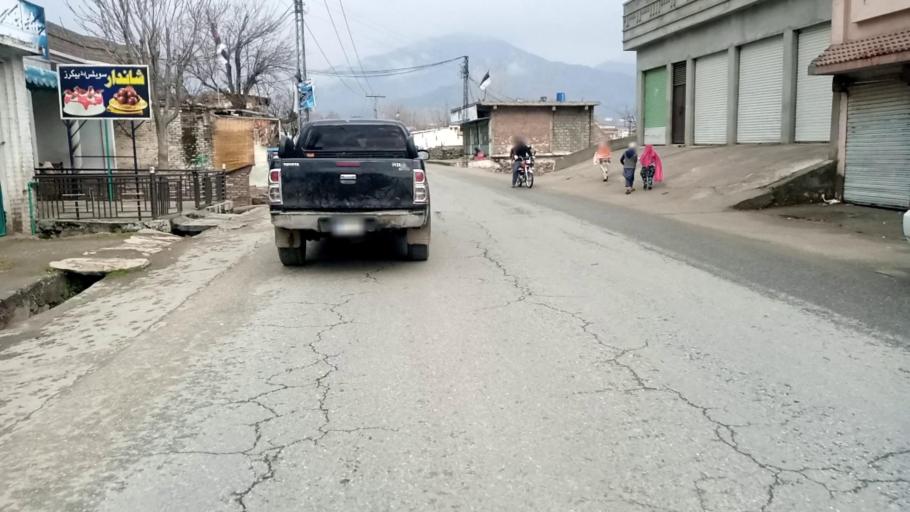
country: PK
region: Khyber Pakhtunkhwa
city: Mingora
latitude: 34.8430
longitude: 72.4171
